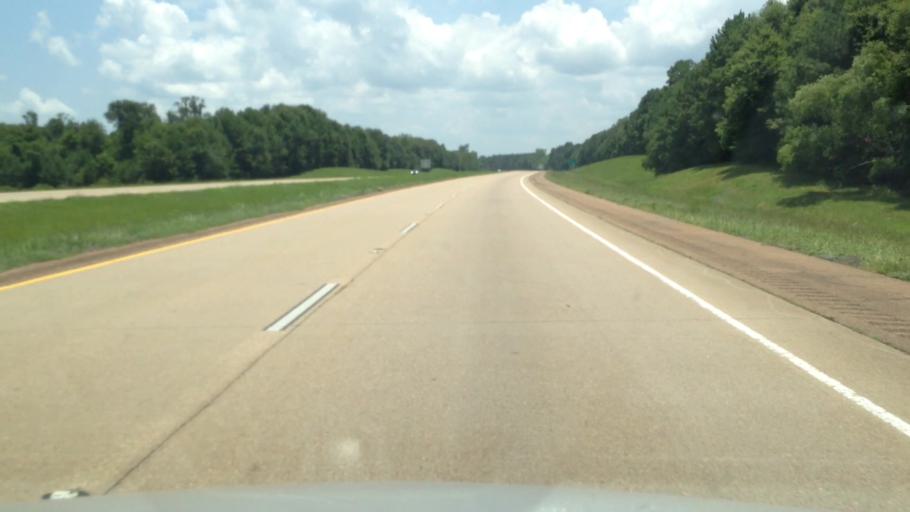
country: US
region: Louisiana
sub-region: Rapides Parish
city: Woodworth
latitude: 31.1524
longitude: -92.4539
